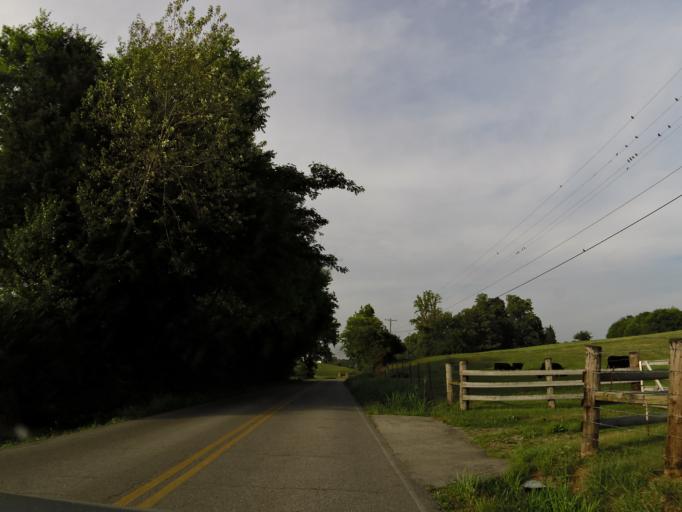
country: US
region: Tennessee
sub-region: Blount County
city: Wildwood
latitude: 35.8241
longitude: -83.8537
